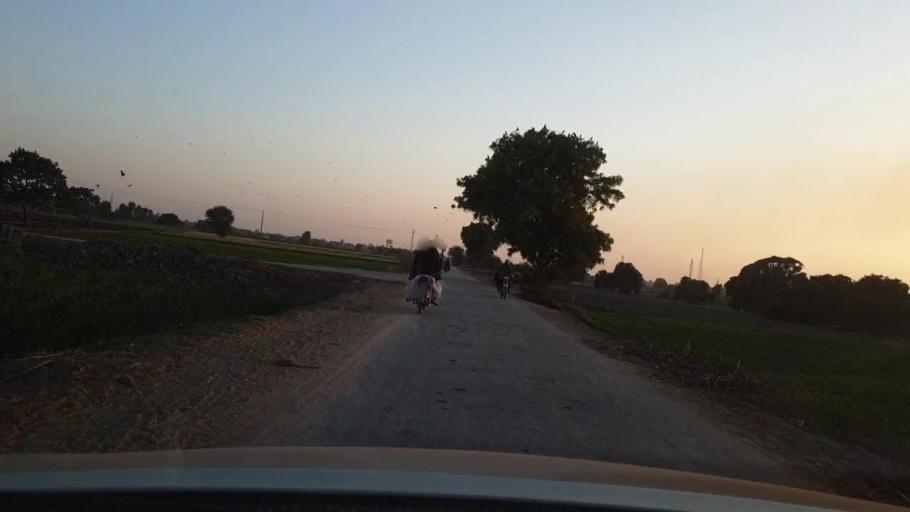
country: PK
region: Sindh
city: Tando Allahyar
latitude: 25.5258
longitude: 68.6239
